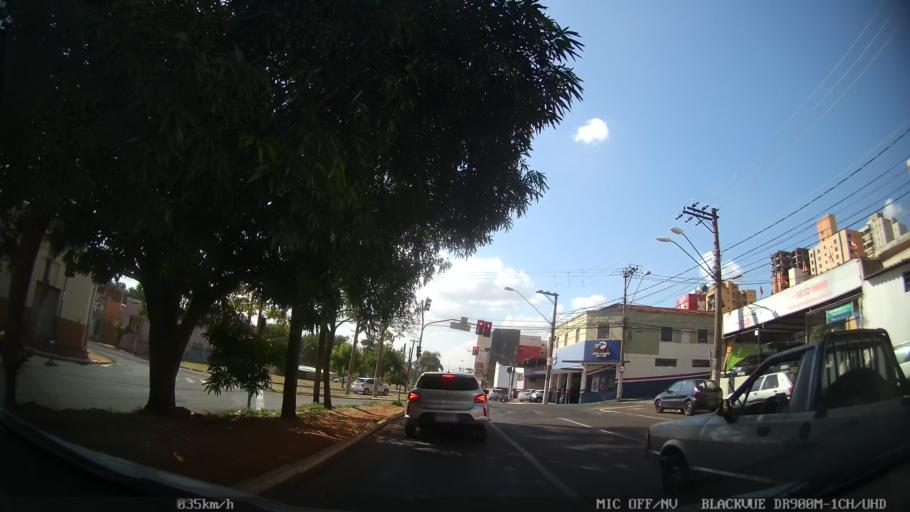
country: BR
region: Sao Paulo
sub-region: Ribeirao Preto
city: Ribeirao Preto
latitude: -21.1791
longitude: -47.8166
